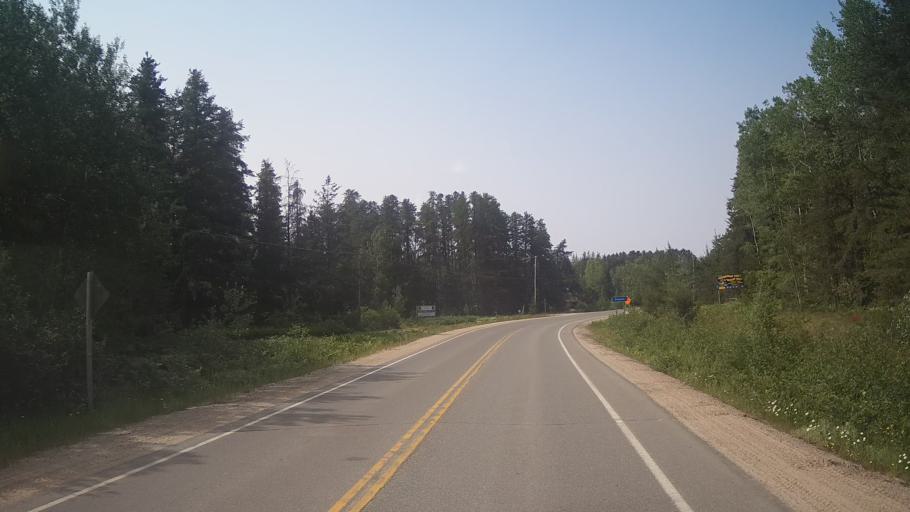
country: CA
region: Ontario
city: Timmins
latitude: 47.6792
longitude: -81.7160
